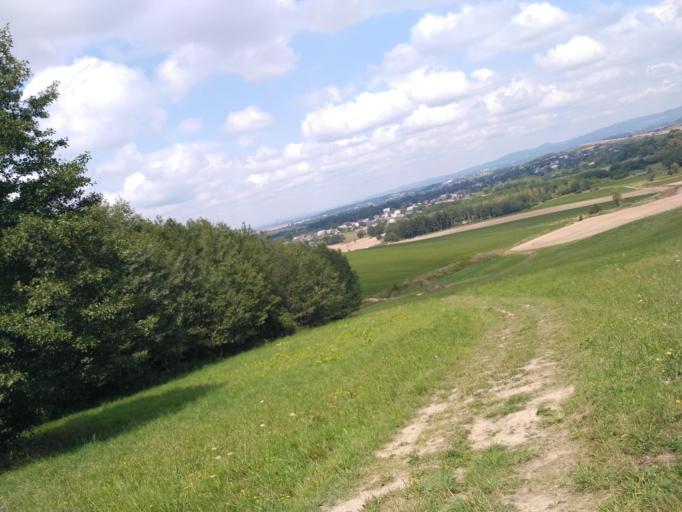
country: PL
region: Subcarpathian Voivodeship
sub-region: Powiat krosnienski
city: Iwonicz-Zdroj
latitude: 49.5890
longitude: 21.8080
